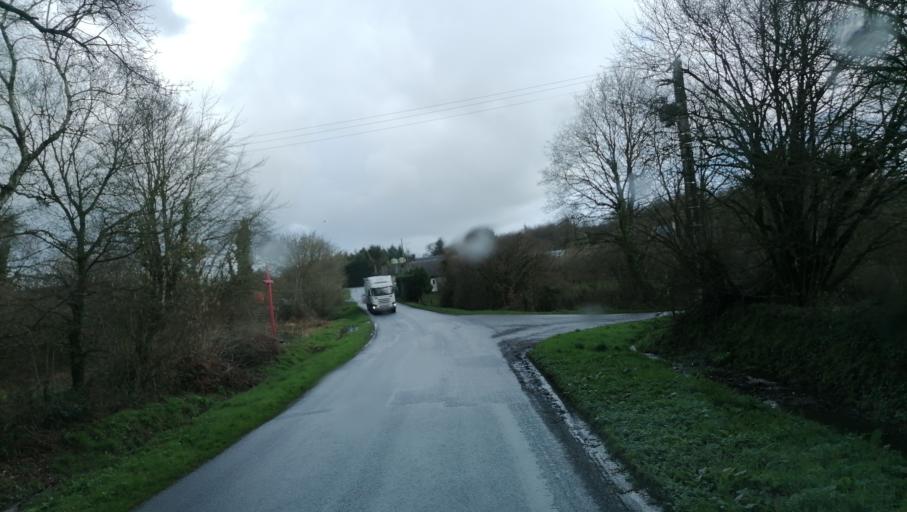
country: FR
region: Brittany
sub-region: Departement des Cotes-d'Armor
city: Lanrodec
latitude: 48.5061
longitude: -3.0292
